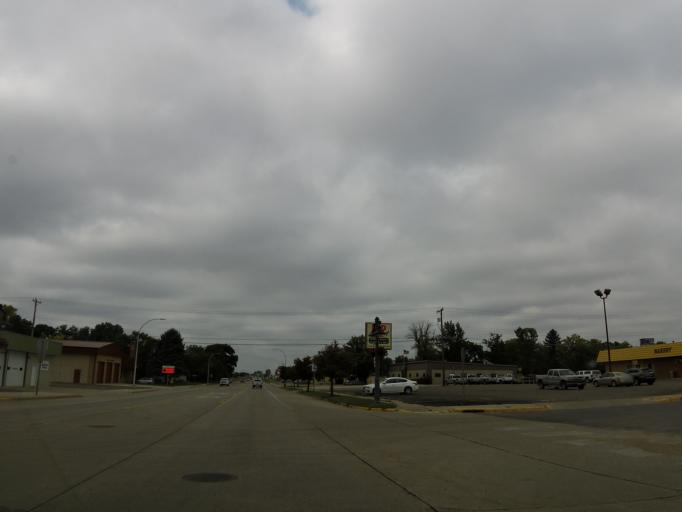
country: US
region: Minnesota
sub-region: Renville County
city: Olivia
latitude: 44.7765
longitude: -94.9908
